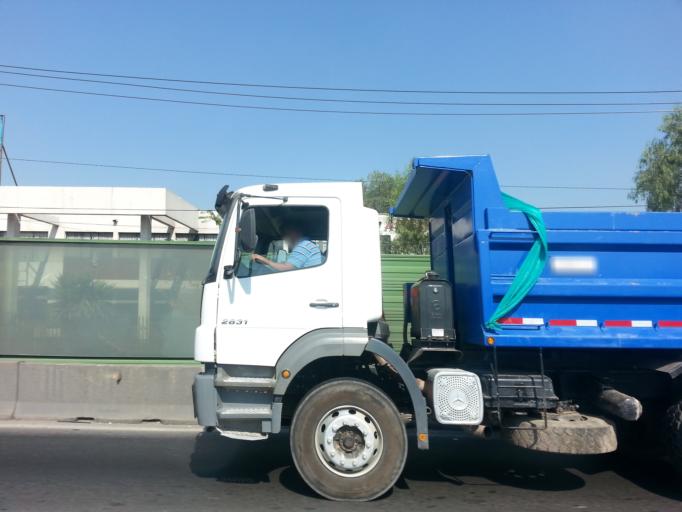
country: CL
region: Santiago Metropolitan
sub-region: Provincia de Santiago
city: La Pintana
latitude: -33.5400
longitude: -70.6524
